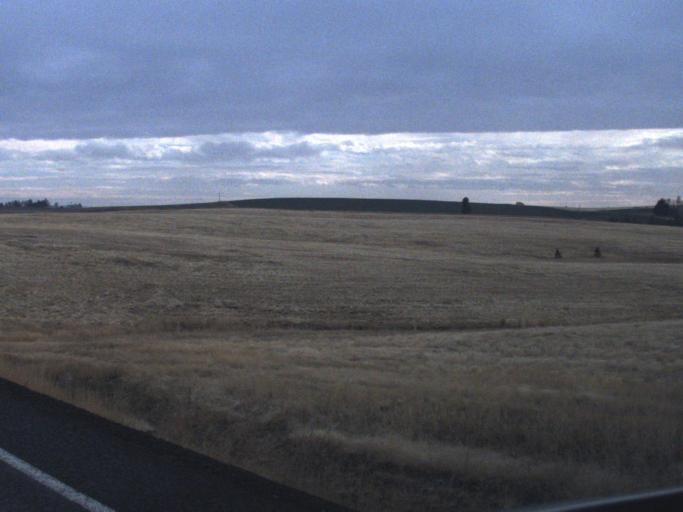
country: US
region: Washington
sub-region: Lincoln County
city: Davenport
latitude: 47.8087
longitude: -118.1776
